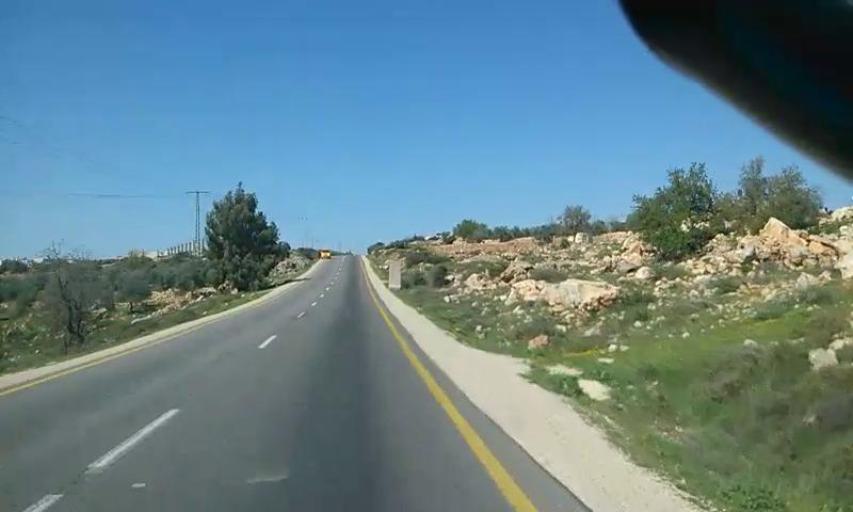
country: PS
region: West Bank
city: Jurat ash Sham`ah
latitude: 31.6481
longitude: 35.1712
